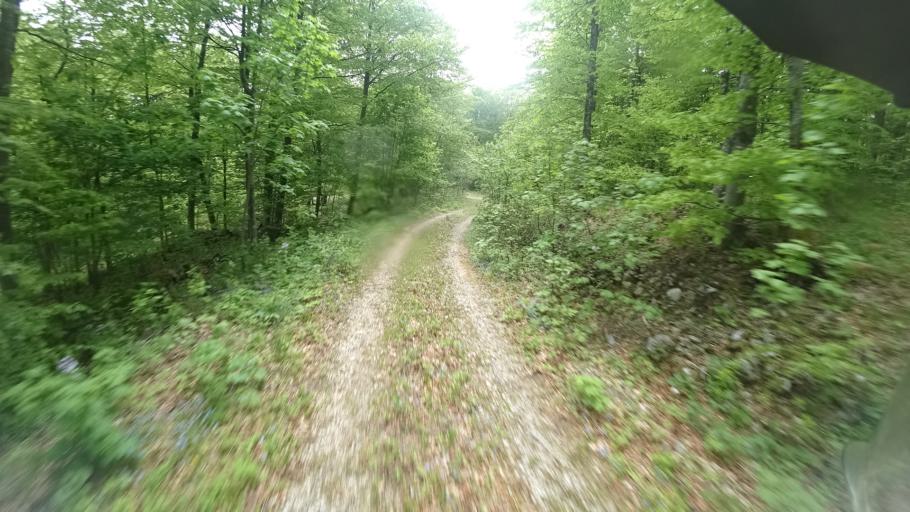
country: BA
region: Federation of Bosnia and Herzegovina
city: Orasac
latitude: 44.5675
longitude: 15.8803
